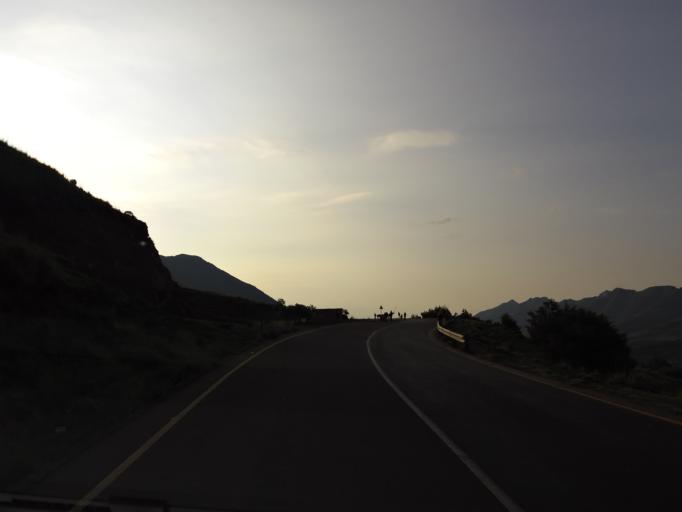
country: LS
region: Butha-Buthe
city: Butha-Buthe
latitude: -29.0454
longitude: 28.3197
